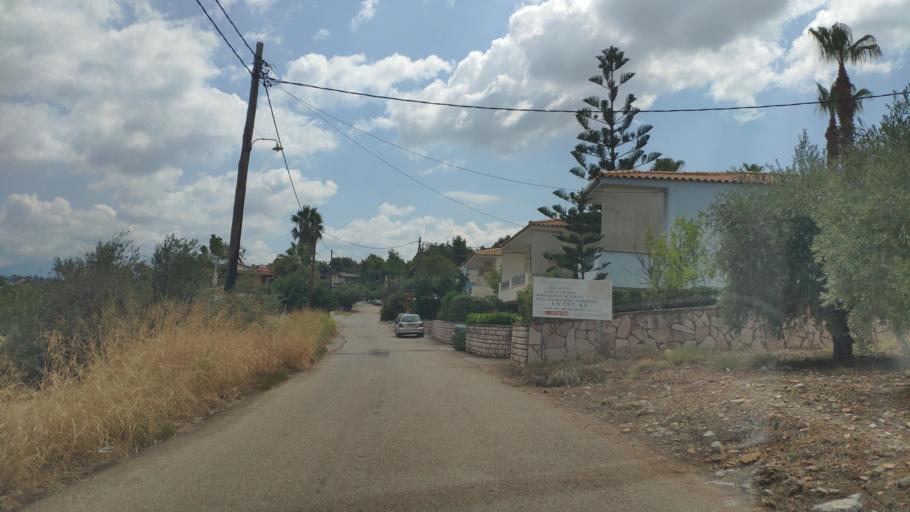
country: GR
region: Central Greece
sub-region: Nomos Fthiotidos
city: Malesina
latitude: 38.6475
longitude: 23.1903
